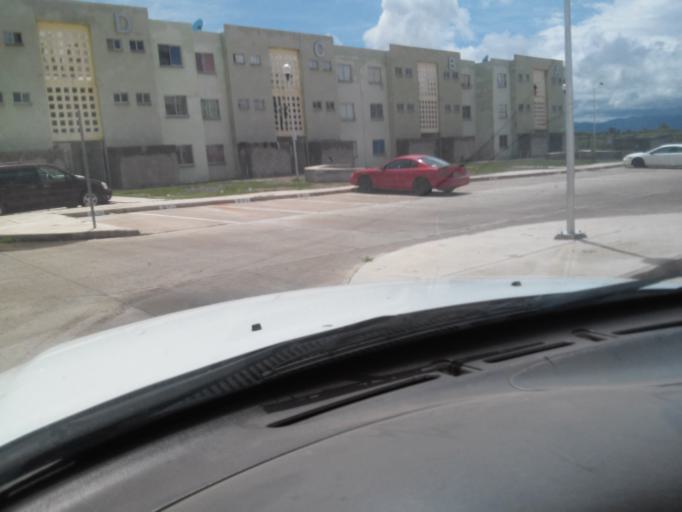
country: MX
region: Durango
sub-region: Durango
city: Jose Refugio Salcido
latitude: 24.0157
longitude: -104.5454
